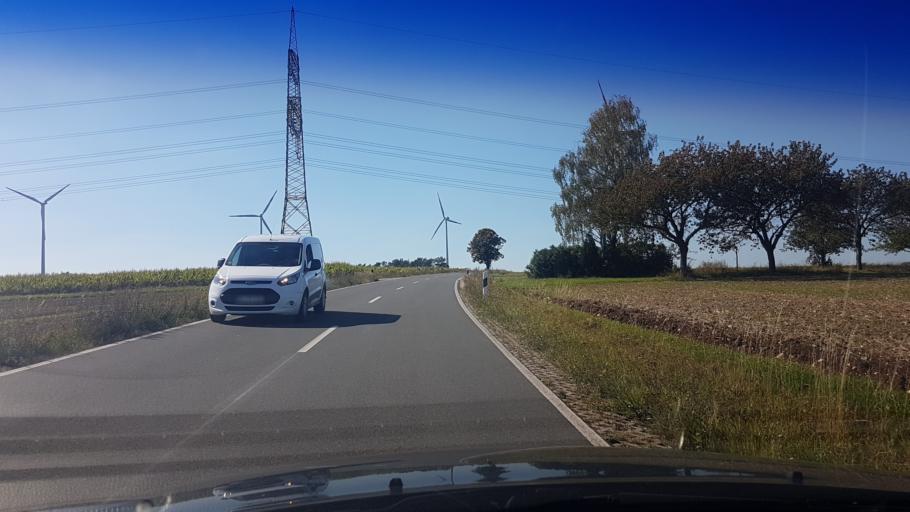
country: DE
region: Bavaria
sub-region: Upper Franconia
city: Heiligenstadt
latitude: 49.8546
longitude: 11.1067
